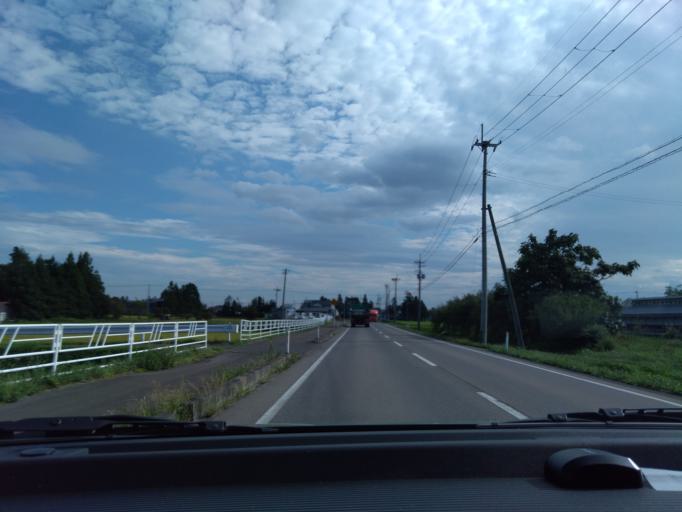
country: JP
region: Iwate
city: Hanamaki
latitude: 39.4489
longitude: 141.0977
